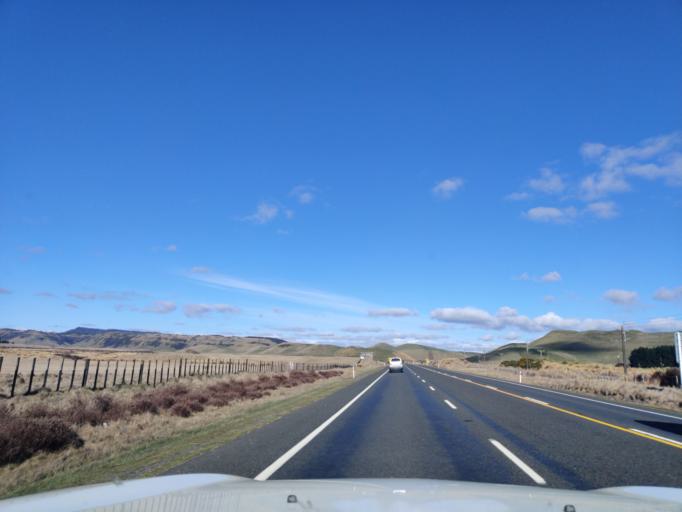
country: NZ
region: Manawatu-Wanganui
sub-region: Ruapehu District
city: Waiouru
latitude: -39.4910
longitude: 175.6711
